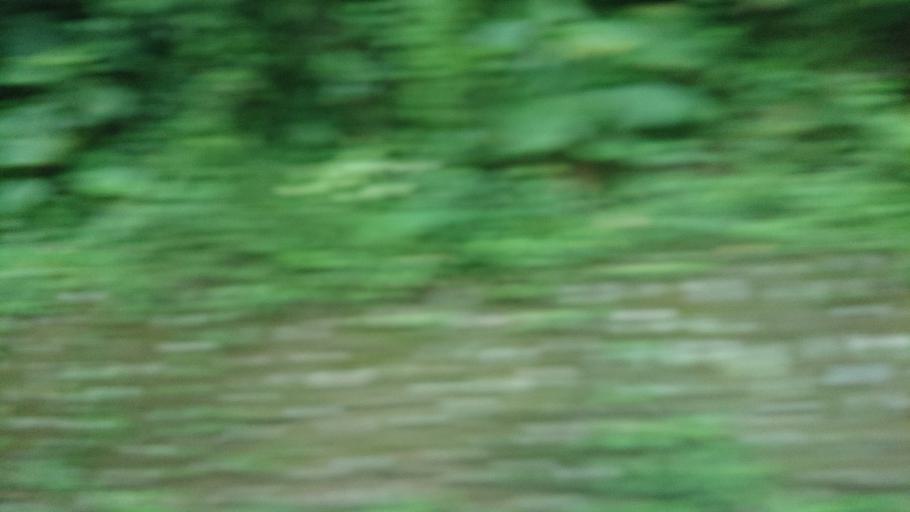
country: TW
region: Taiwan
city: Daxi
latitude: 24.8901
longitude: 121.3770
